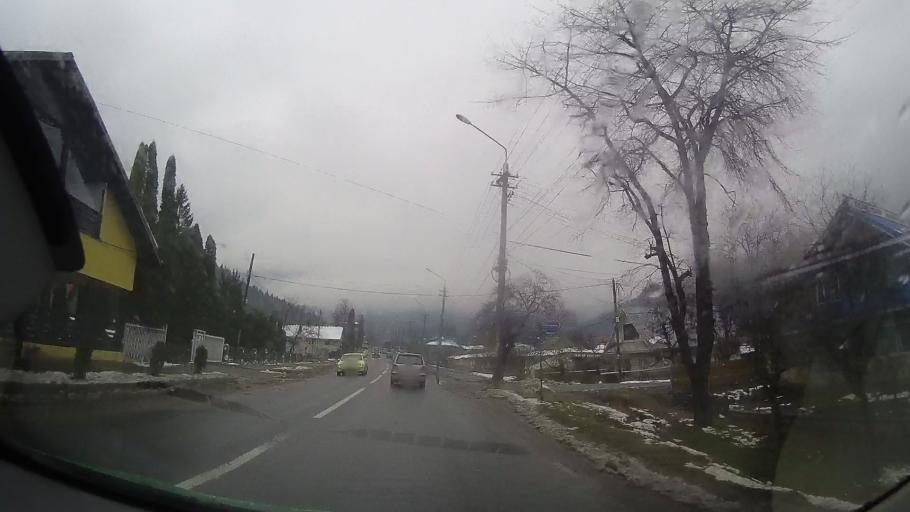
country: RO
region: Neamt
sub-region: Comuna Bicaz
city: Dodeni
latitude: 46.9081
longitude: 26.1029
